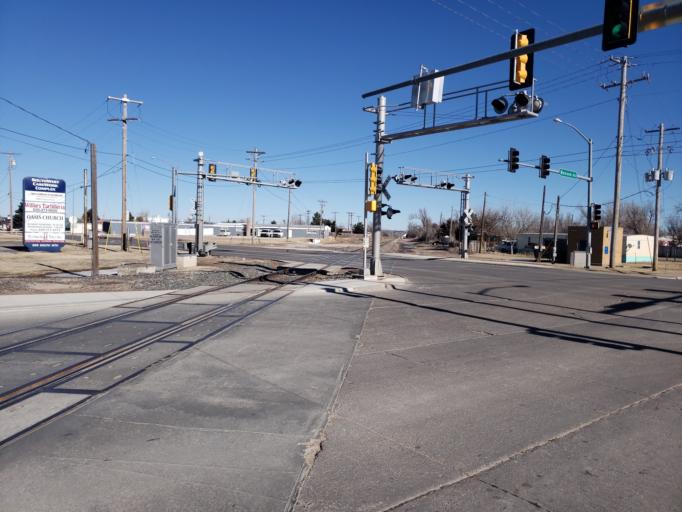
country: US
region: Kansas
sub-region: Ford County
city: Dodge City
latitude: 37.7364
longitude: -100.0334
